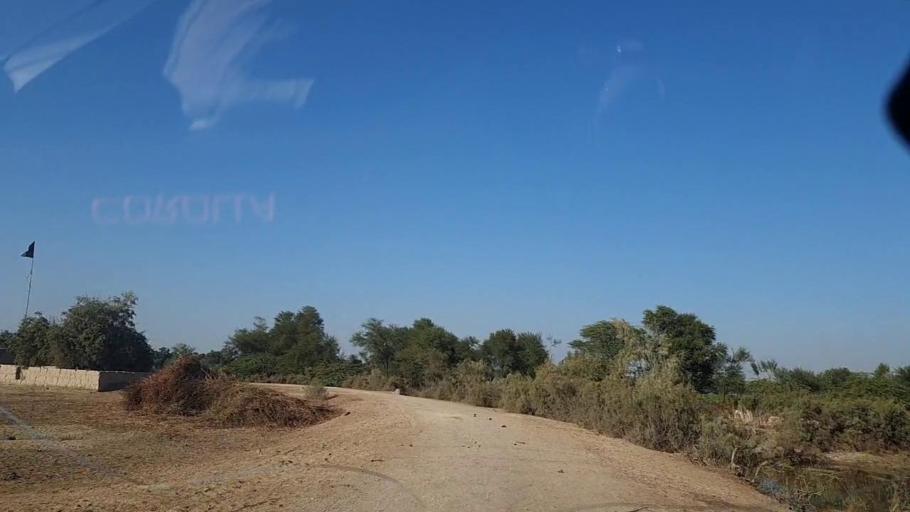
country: PK
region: Sindh
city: Khanpur
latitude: 27.7679
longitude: 69.2944
